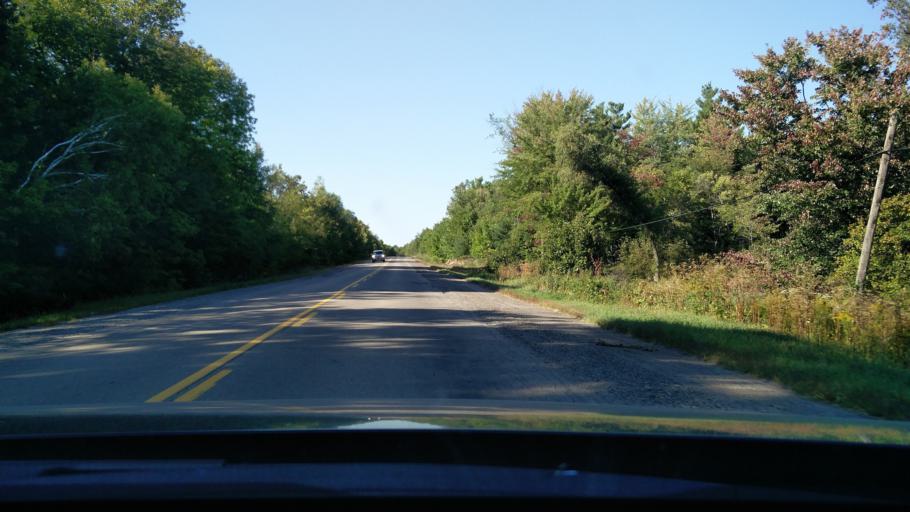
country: CA
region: Ontario
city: Perth
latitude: 44.7110
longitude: -76.4011
